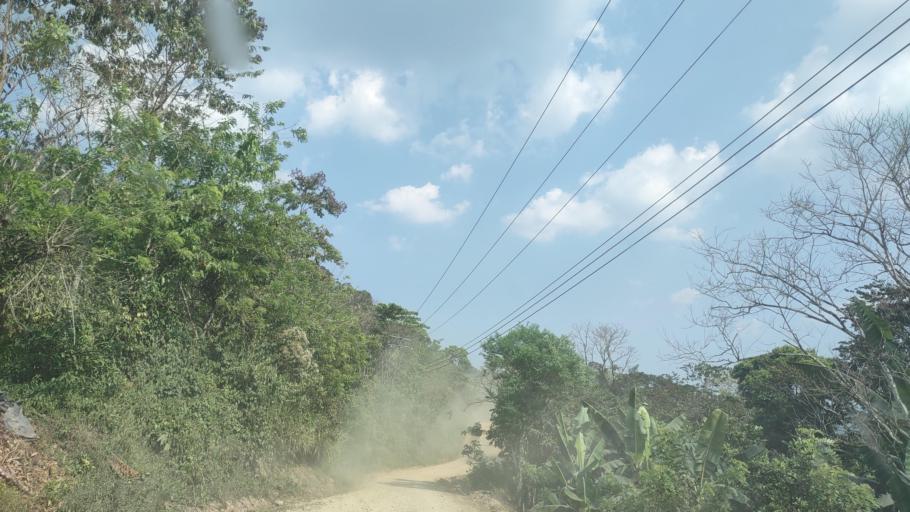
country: MX
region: Chiapas
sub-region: Tecpatan
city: Raudales Malpaso
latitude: 17.3312
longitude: -93.7486
